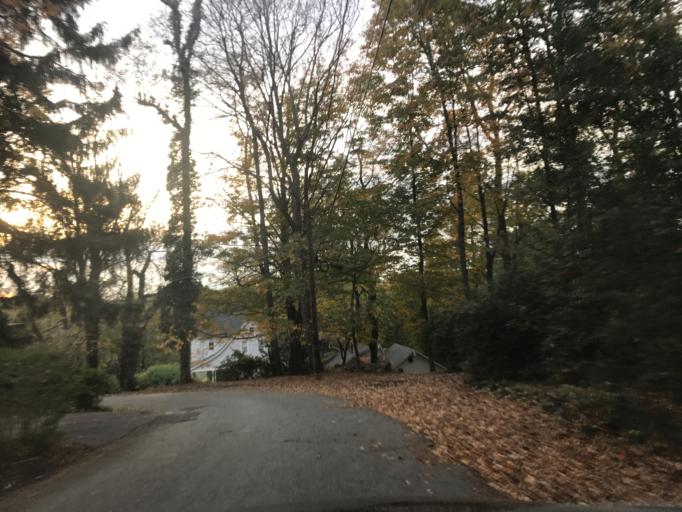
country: US
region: Maryland
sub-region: Baltimore County
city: Lutherville
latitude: 39.4066
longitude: -76.6431
